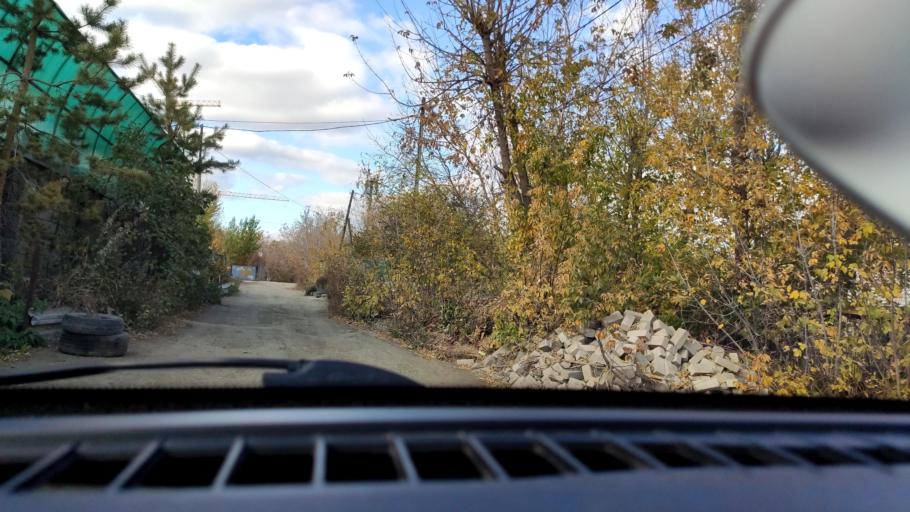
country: RU
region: Samara
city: Samara
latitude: 53.2216
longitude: 50.2088
